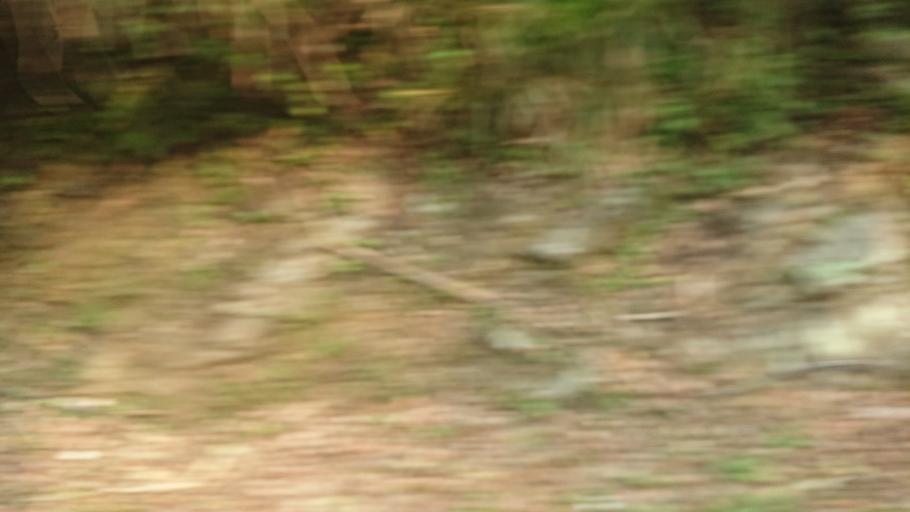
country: TW
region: Taiwan
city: Daxi
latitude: 24.8744
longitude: 121.3897
